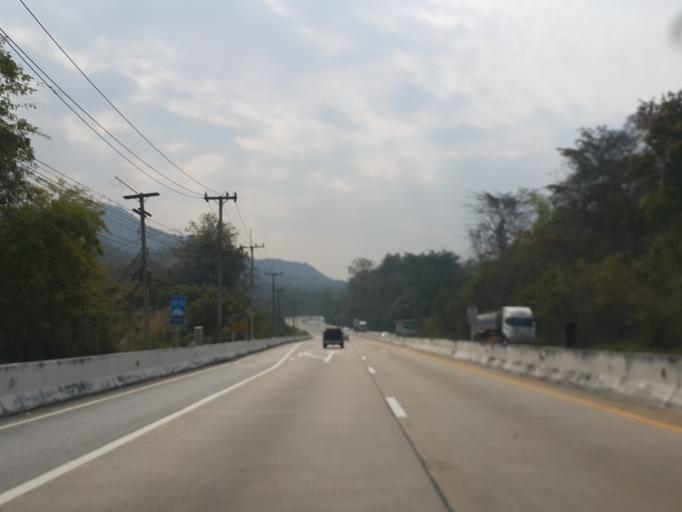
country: TH
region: Lamphun
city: Mae Tha
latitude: 18.4491
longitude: 99.2036
